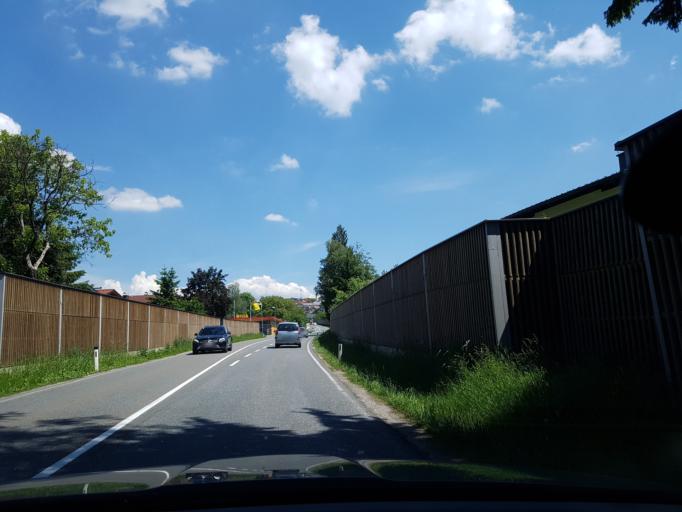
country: AT
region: Salzburg
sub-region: Politischer Bezirk Salzburg-Umgebung
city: Elixhausen
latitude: 47.8602
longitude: 13.0594
